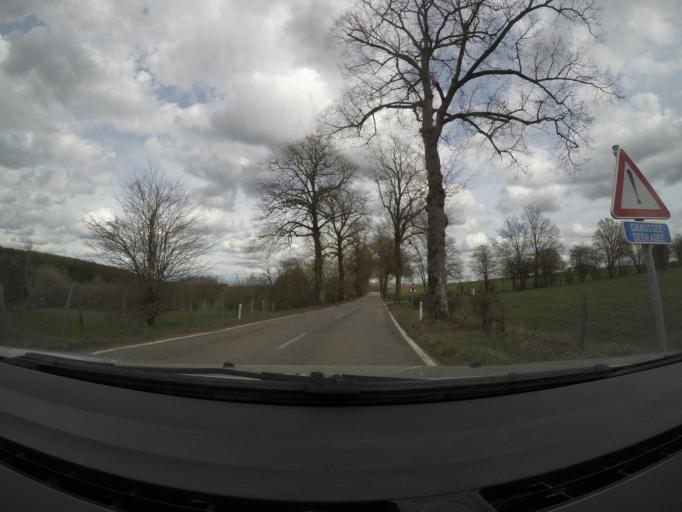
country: BE
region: Wallonia
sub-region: Province du Luxembourg
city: Leglise
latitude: 49.7911
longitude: 5.4910
